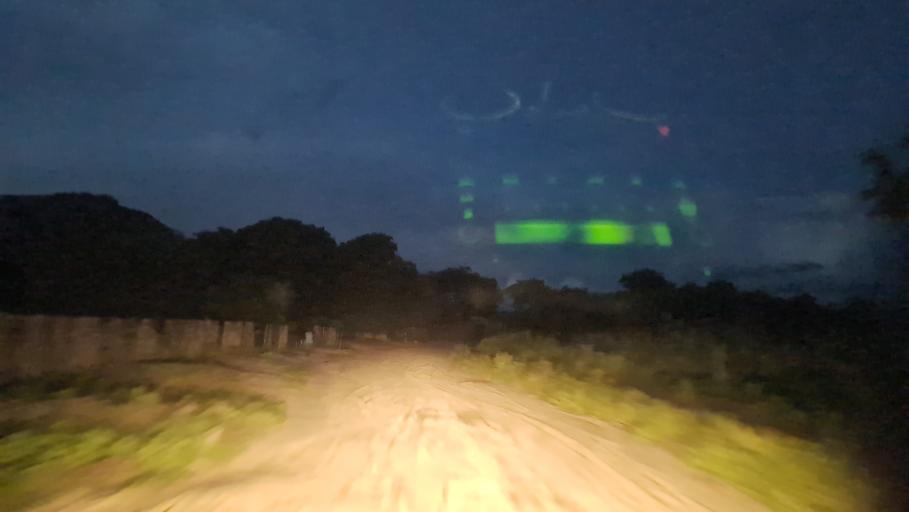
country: MZ
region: Nampula
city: Nampula
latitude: -14.6627
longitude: 39.8378
